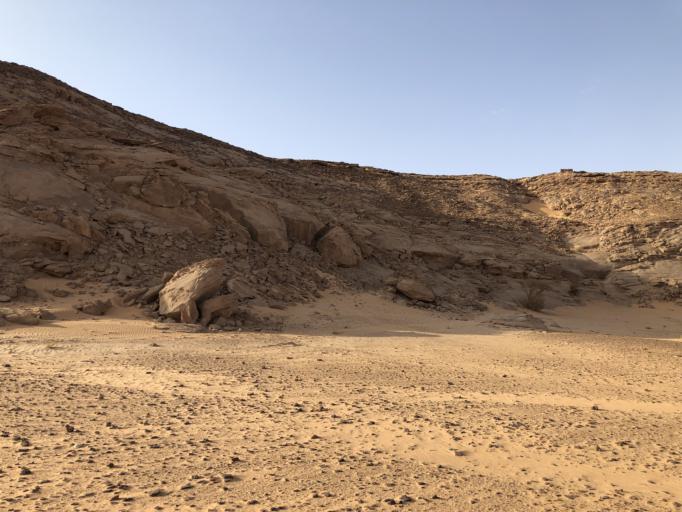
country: SA
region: Ar Riyad
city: shokhaib
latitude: 23.6093
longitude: 46.0762
